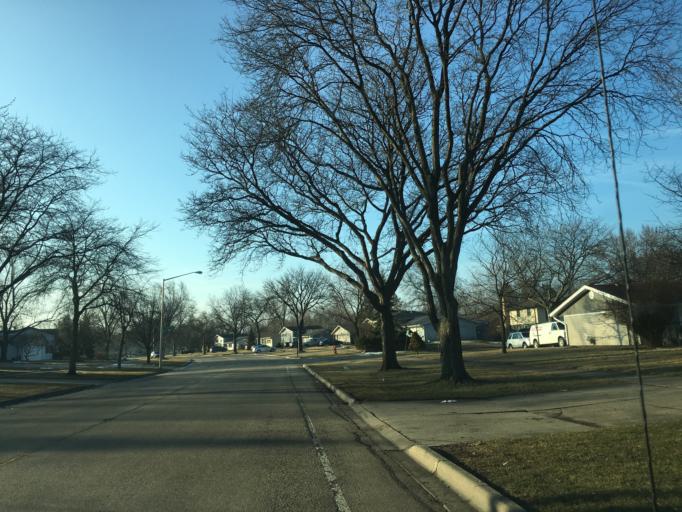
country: US
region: Illinois
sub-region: Cook County
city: Schaumburg
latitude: 42.0203
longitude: -88.1003
